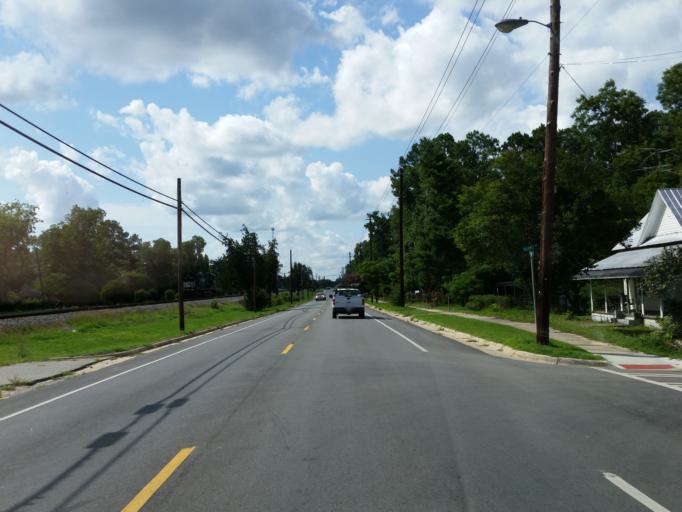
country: US
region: Georgia
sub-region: Turner County
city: Ashburn
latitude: 31.6979
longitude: -83.6494
